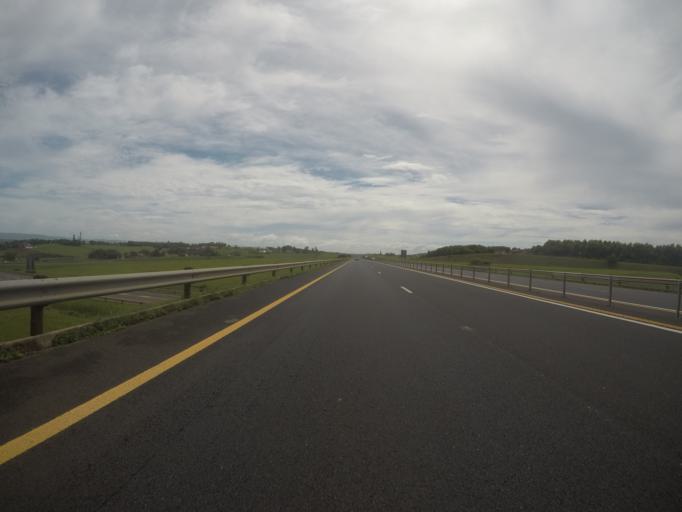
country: ZA
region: KwaZulu-Natal
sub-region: iLembe District Municipality
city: Mandeni
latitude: -29.0777
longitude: 31.6145
